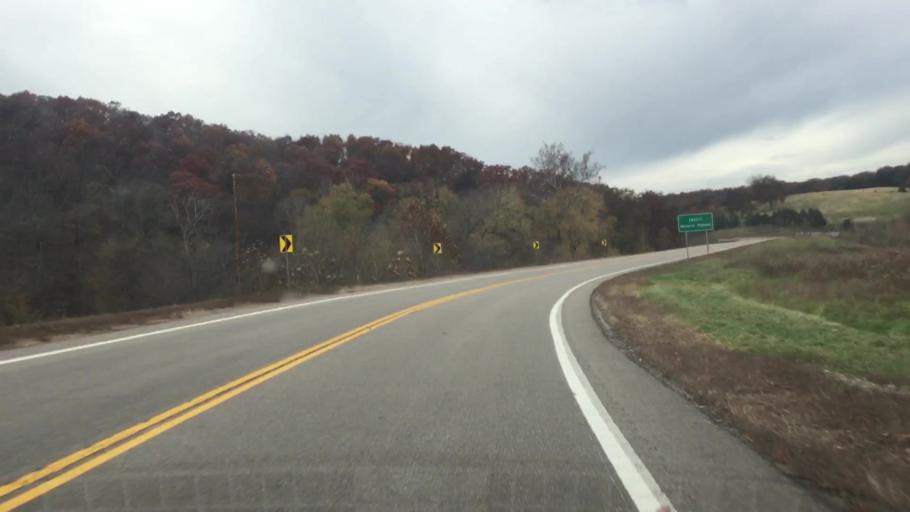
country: US
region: Missouri
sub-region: Gasconade County
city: Hermann
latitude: 38.7181
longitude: -91.6892
